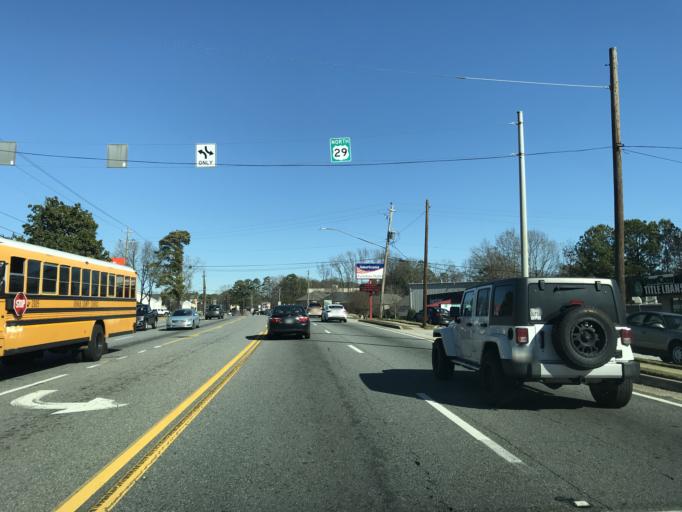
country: US
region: Georgia
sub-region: DeKalb County
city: Tucker
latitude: 33.8380
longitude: -84.2372
